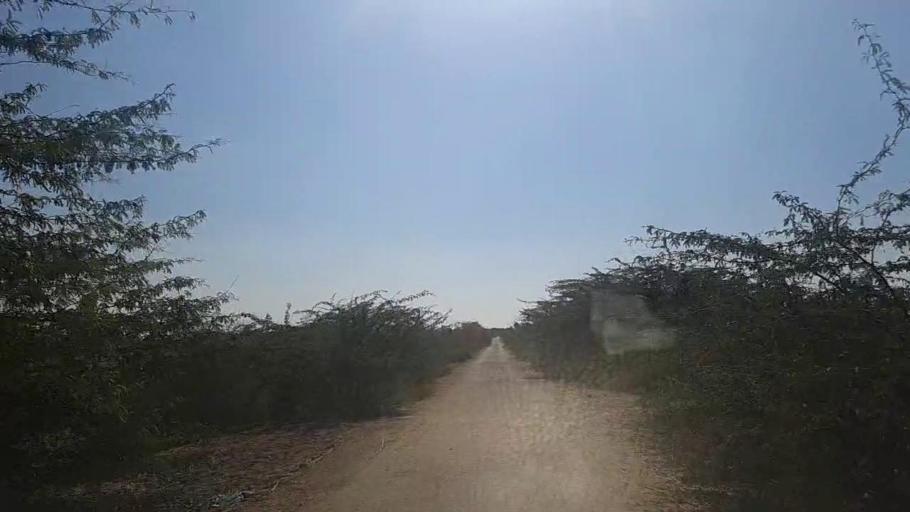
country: PK
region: Sindh
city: Khadro
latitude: 26.1608
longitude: 68.8380
